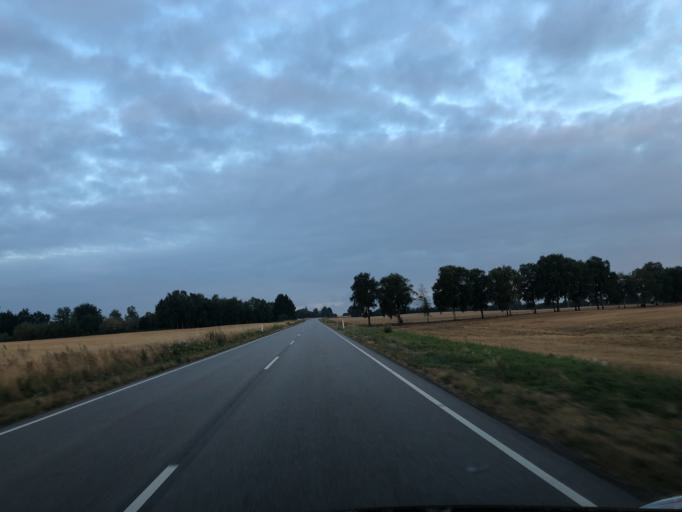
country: DK
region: Zealand
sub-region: Soro Kommune
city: Dianalund
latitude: 55.4821
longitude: 11.4981
